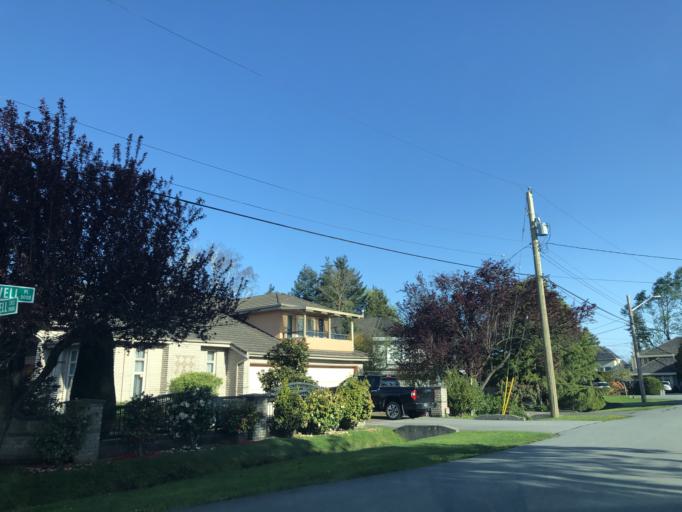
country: CA
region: British Columbia
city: Richmond
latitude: 49.1417
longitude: -123.1170
